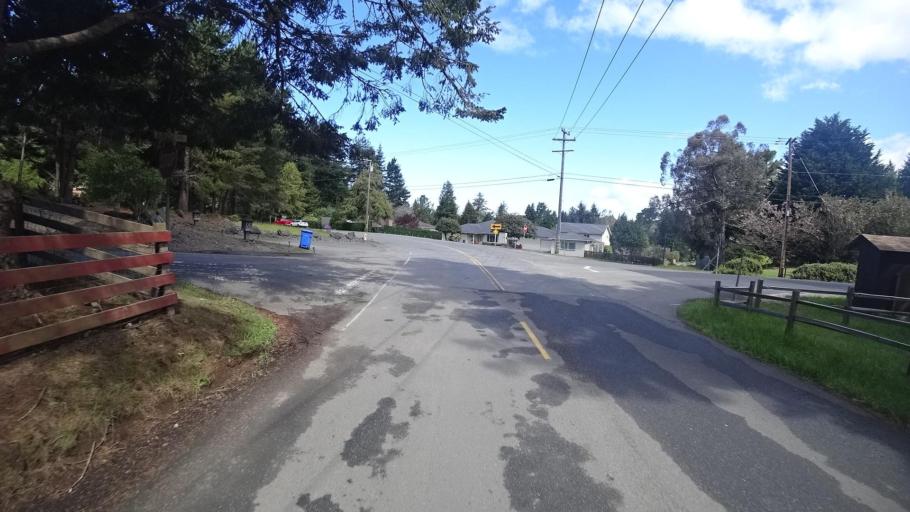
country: US
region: California
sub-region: Humboldt County
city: McKinleyville
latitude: 40.9230
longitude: -124.0802
